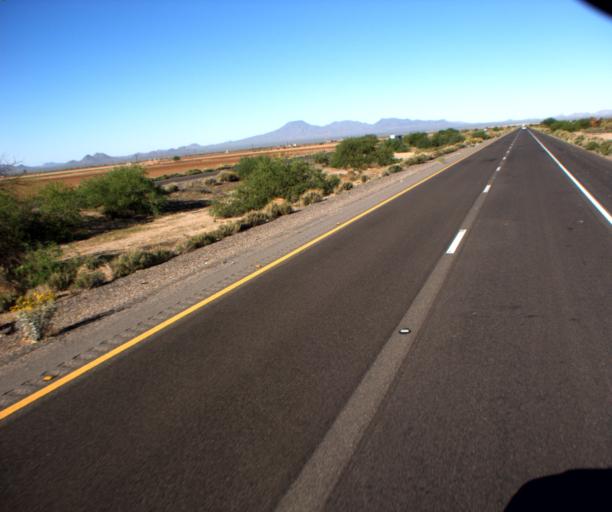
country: US
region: Arizona
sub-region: Pinal County
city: Casa Grande
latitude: 32.8283
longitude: -111.8810
